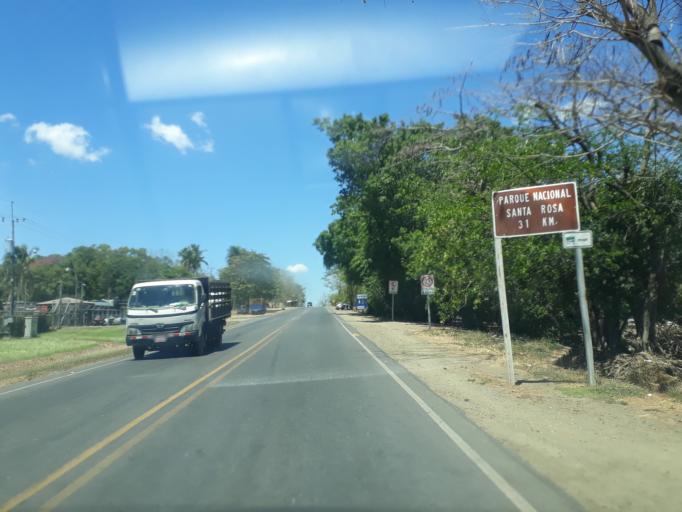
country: CR
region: Guanacaste
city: Liberia
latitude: 10.6616
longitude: -85.4709
